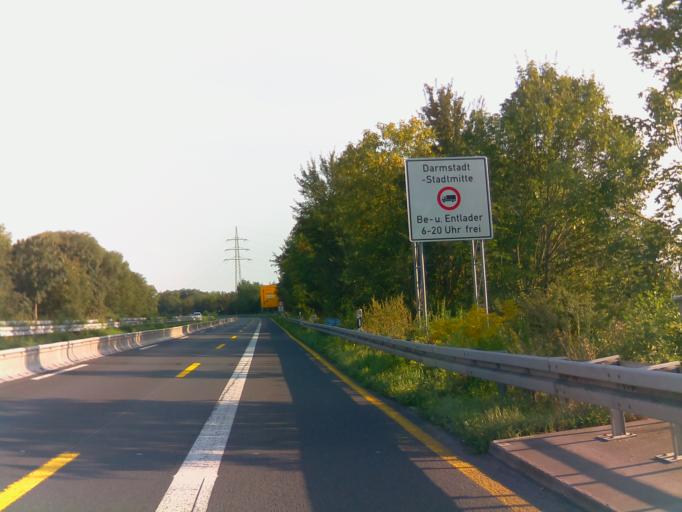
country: DE
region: Hesse
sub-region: Regierungsbezirk Darmstadt
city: Munster
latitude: 49.9205
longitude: 8.8458
